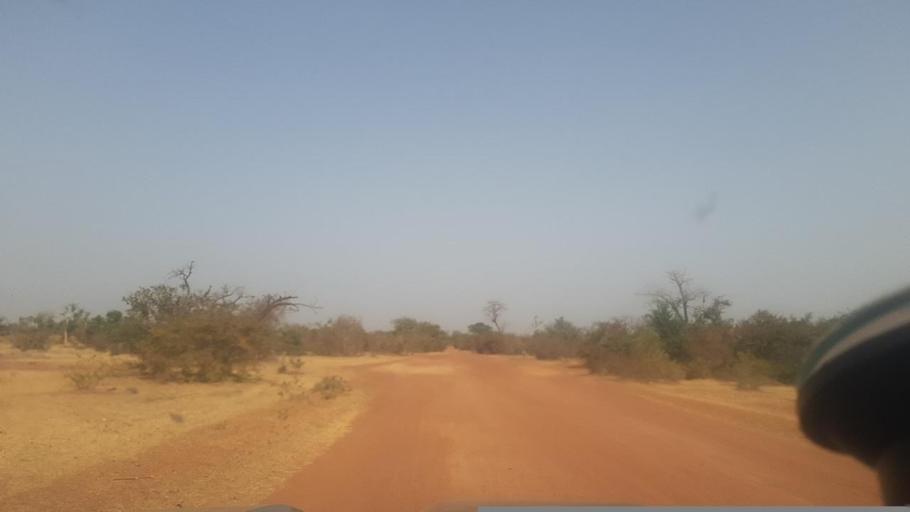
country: ML
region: Segou
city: Bla
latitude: 12.8581
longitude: -5.9700
